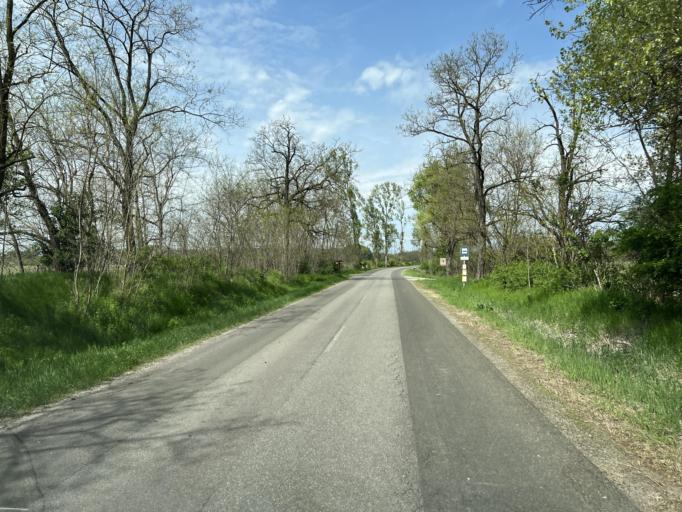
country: HU
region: Pest
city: Albertirsa
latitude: 47.2008
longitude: 19.6115
